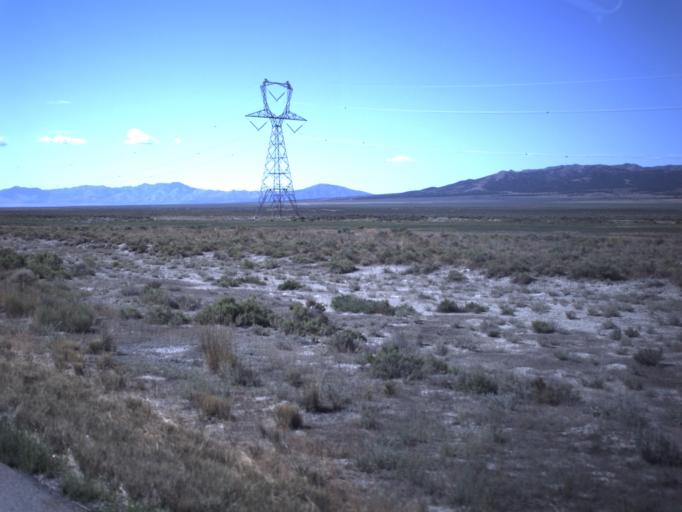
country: US
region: Utah
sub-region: Tooele County
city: Tooele
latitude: 40.3043
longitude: -112.4033
